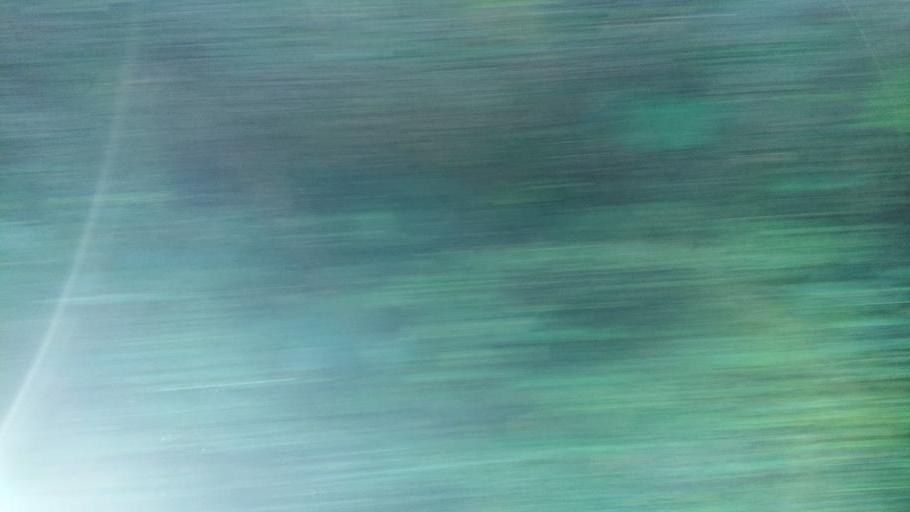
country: TW
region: Taiwan
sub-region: Chiayi
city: Jiayi Shi
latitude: 23.5248
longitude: 120.6324
